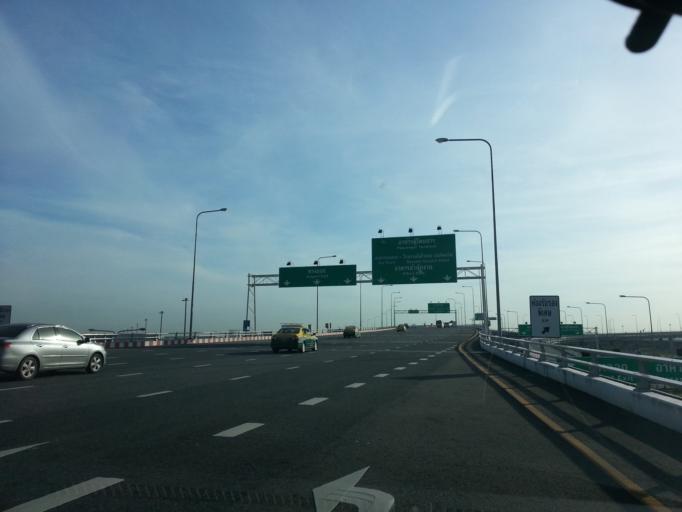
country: TH
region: Bangkok
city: Lat Krabang
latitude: 13.6972
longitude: 100.7494
